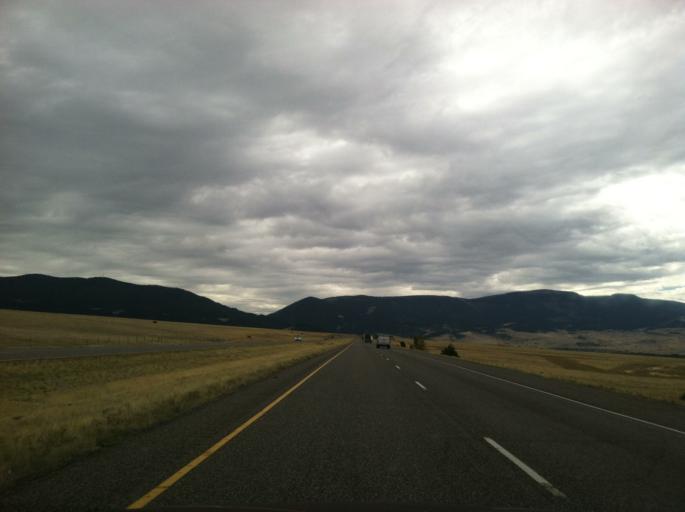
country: US
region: Montana
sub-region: Park County
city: Livingston
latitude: 45.6631
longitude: -110.5291
